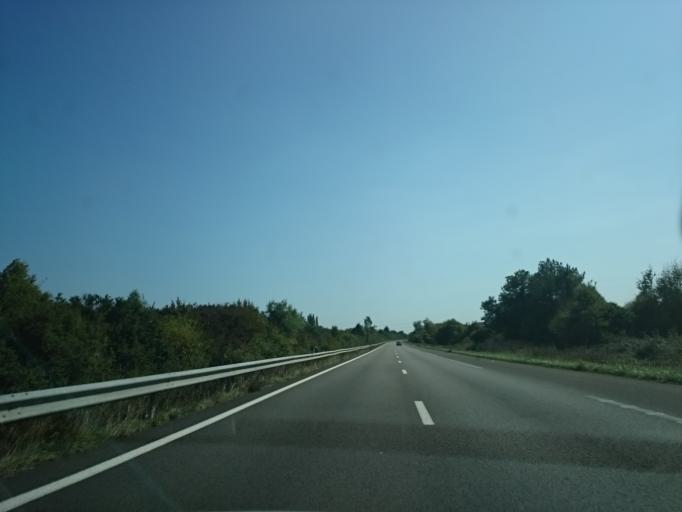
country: FR
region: Pays de la Loire
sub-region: Departement de la Loire-Atlantique
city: Heric
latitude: 47.4345
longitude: -1.6390
